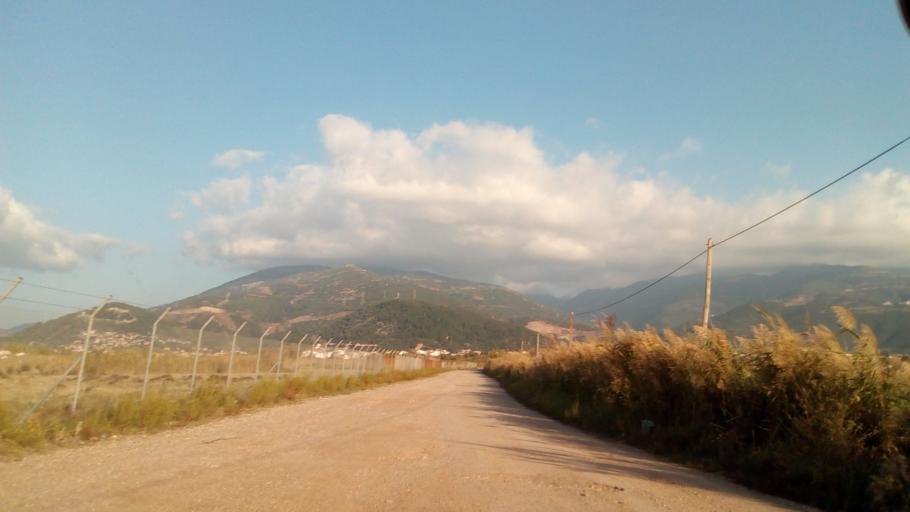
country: GR
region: West Greece
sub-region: Nomos Aitolias kai Akarnanias
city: Nafpaktos
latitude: 38.3809
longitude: 21.8515
